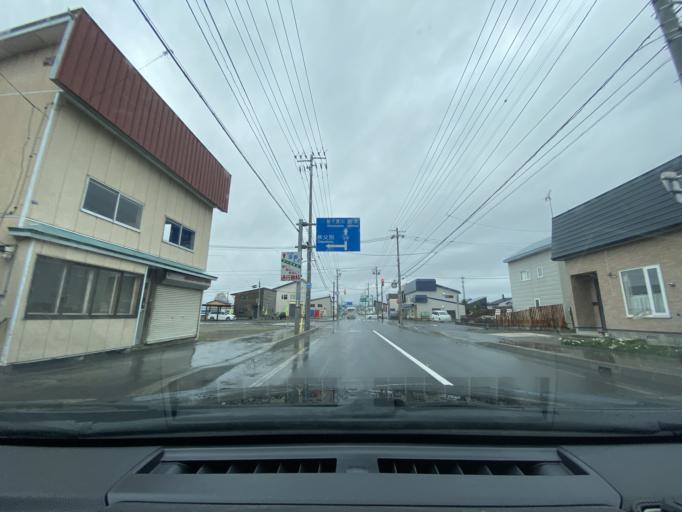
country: JP
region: Hokkaido
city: Fukagawa
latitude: 43.8084
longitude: 141.9424
